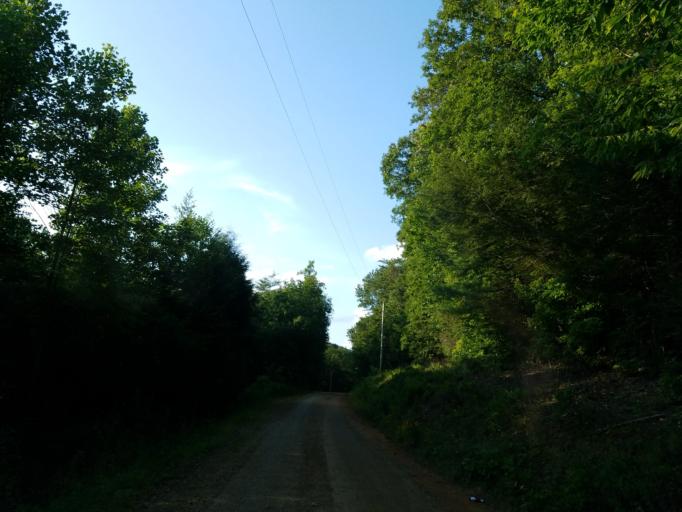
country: US
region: Georgia
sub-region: Lumpkin County
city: Dahlonega
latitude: 34.6616
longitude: -84.0876
